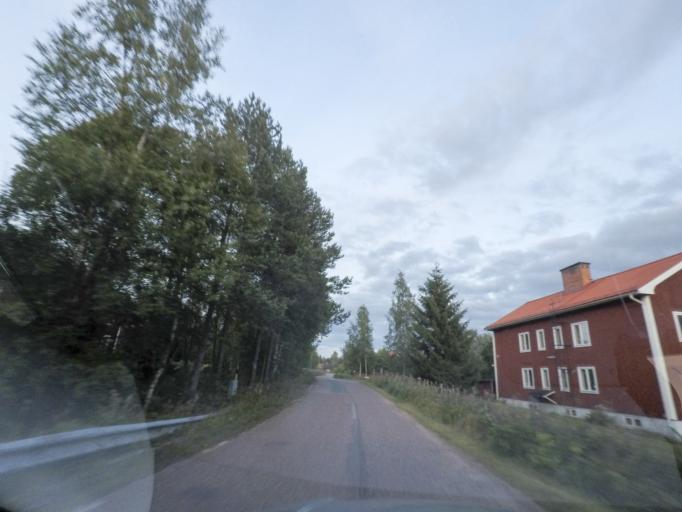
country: SE
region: OErebro
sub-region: Hallefors Kommun
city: Haellefors
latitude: 60.0407
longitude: 14.5208
